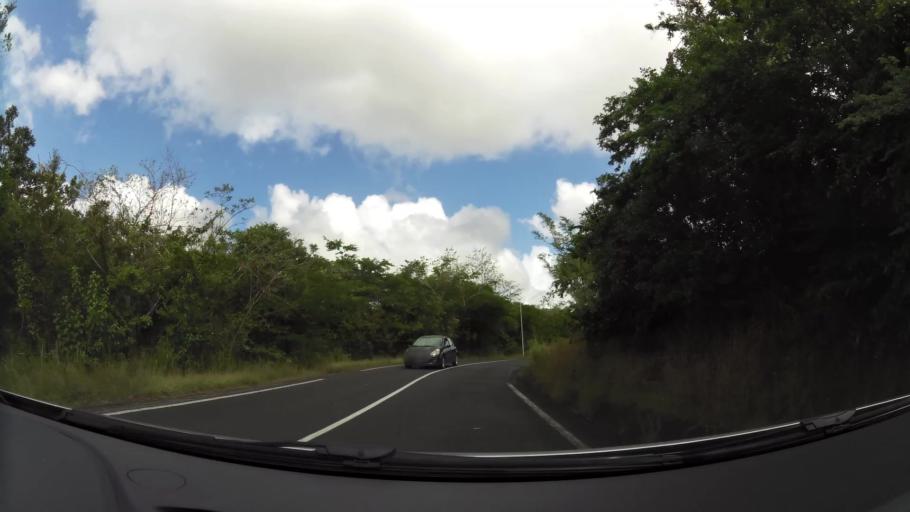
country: MQ
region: Martinique
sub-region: Martinique
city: Sainte-Luce
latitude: 14.4862
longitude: -60.9916
